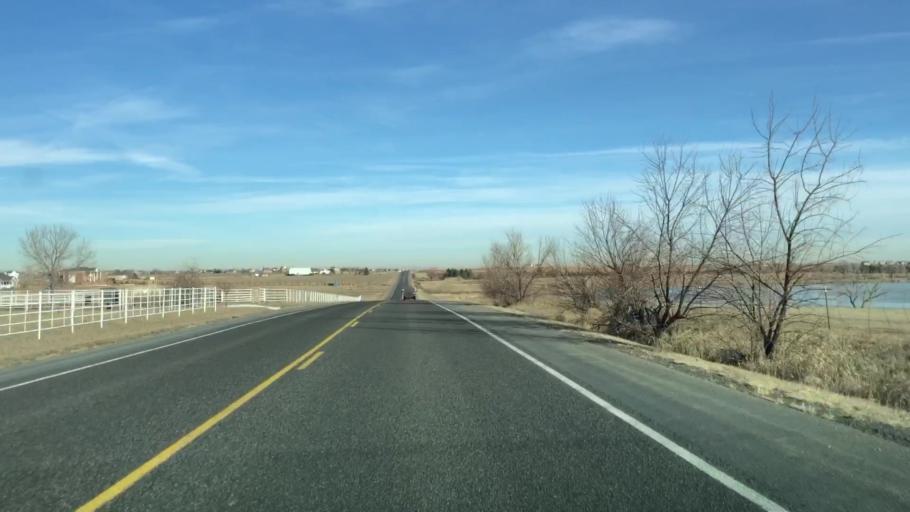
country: US
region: Colorado
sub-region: Weld County
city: Windsor
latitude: 40.4224
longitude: -104.9443
